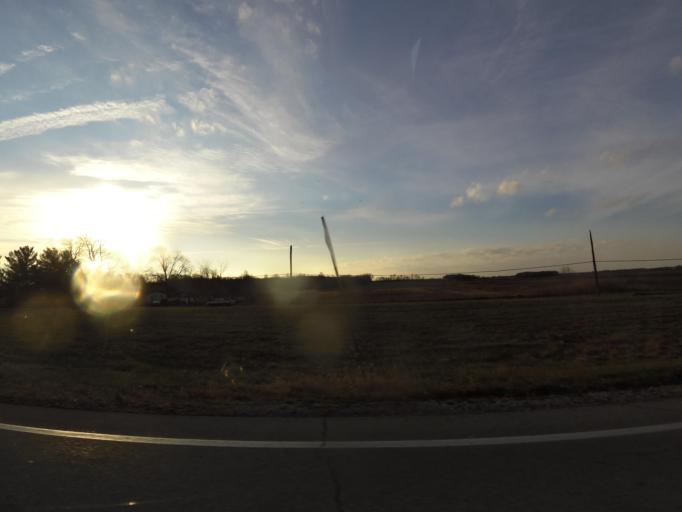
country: US
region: Illinois
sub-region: Fayette County
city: Vandalia
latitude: 38.9558
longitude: -89.1296
